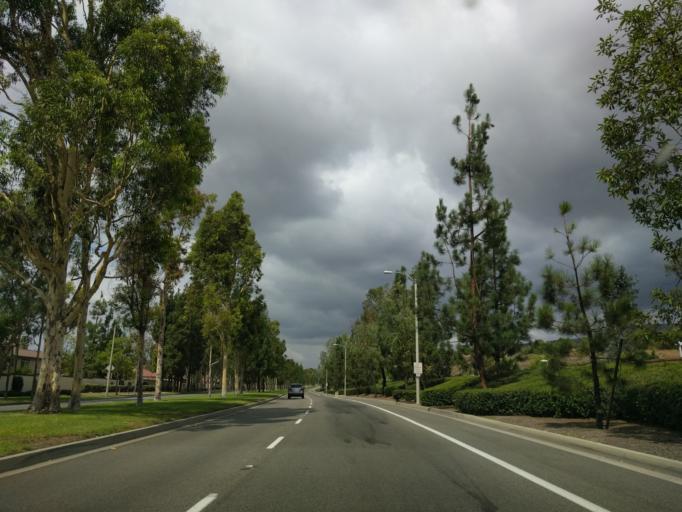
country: US
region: California
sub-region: Orange County
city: North Tustin
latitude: 33.7492
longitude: -117.7668
